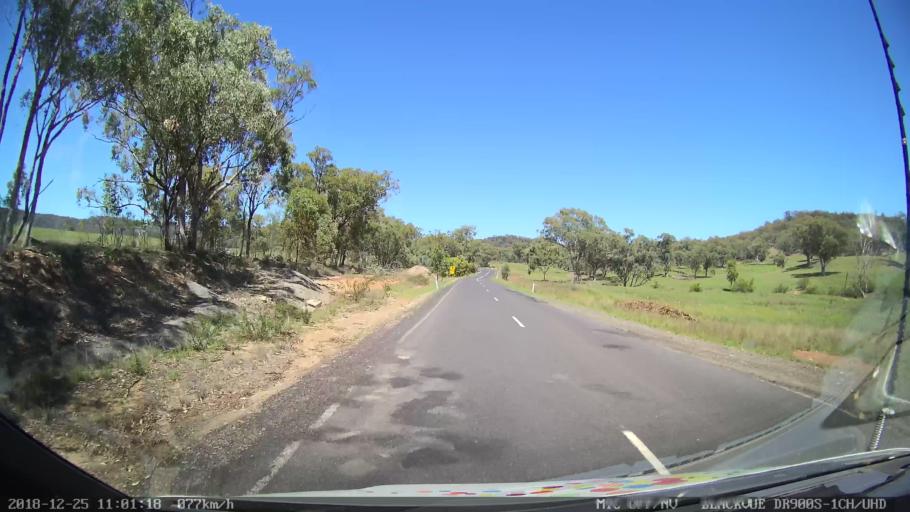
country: AU
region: New South Wales
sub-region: Upper Hunter Shire
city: Merriwa
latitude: -32.4042
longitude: 150.2035
